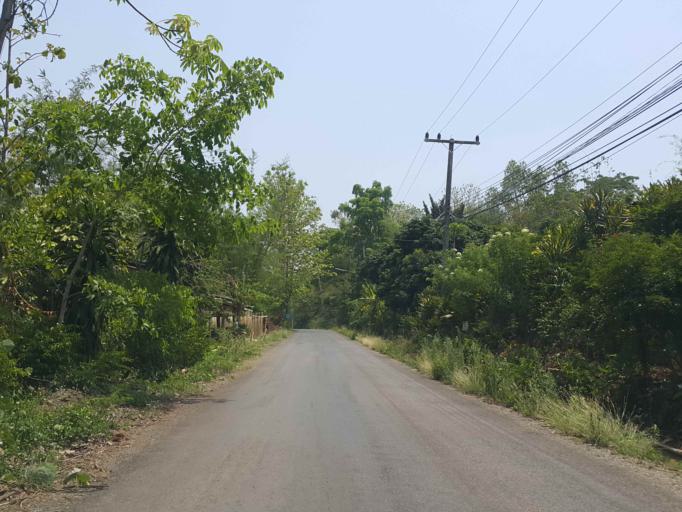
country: TH
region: Chiang Mai
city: Mae Taeng
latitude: 19.1528
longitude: 98.8590
